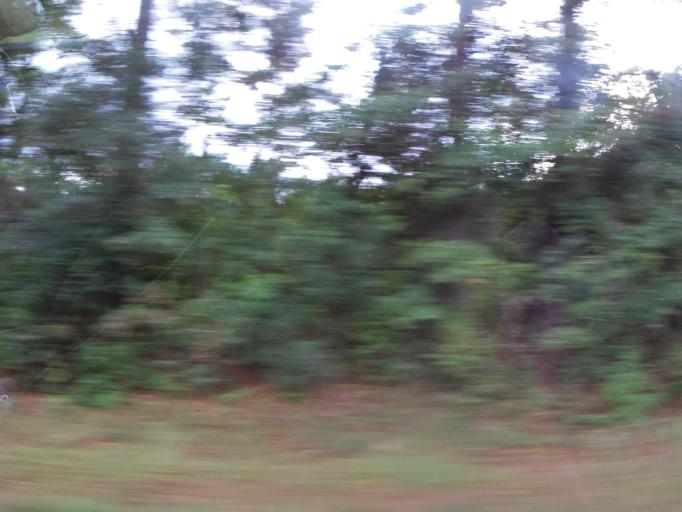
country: US
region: Georgia
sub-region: Liberty County
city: Midway
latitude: 31.8571
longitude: -81.4275
